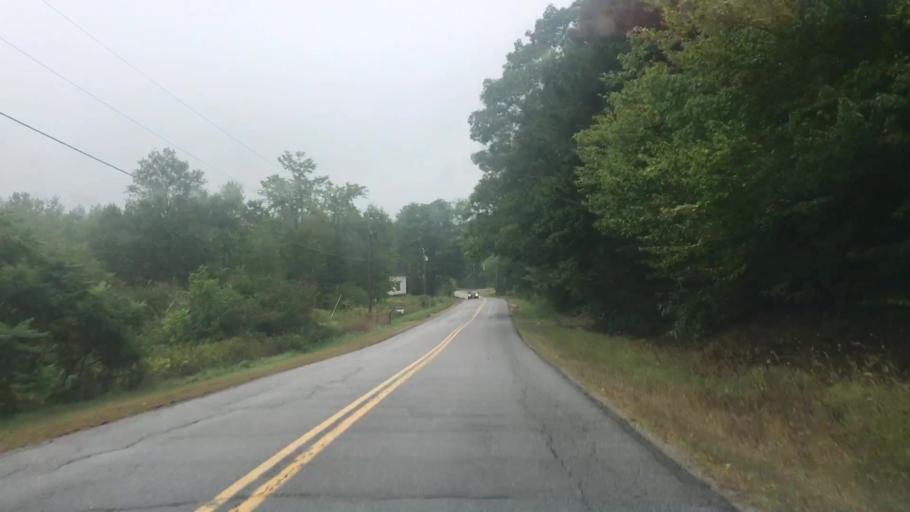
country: US
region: Maine
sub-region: Waldo County
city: Stockton Springs
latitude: 44.5402
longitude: -68.9012
